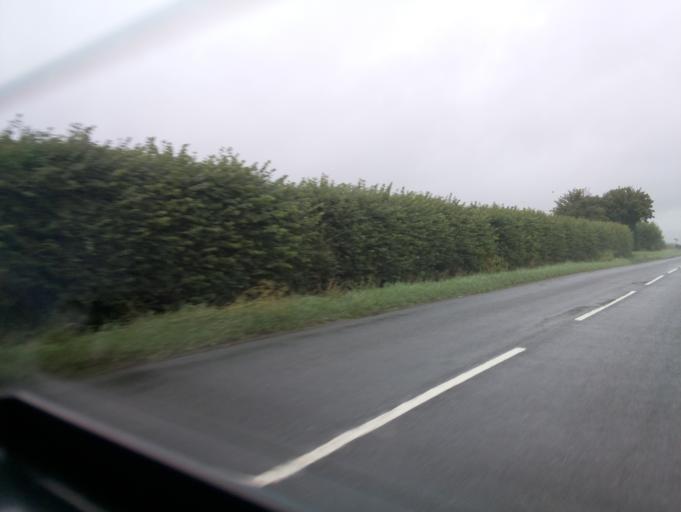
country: GB
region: England
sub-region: Gloucestershire
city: Uckington
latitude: 51.9197
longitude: -2.1406
